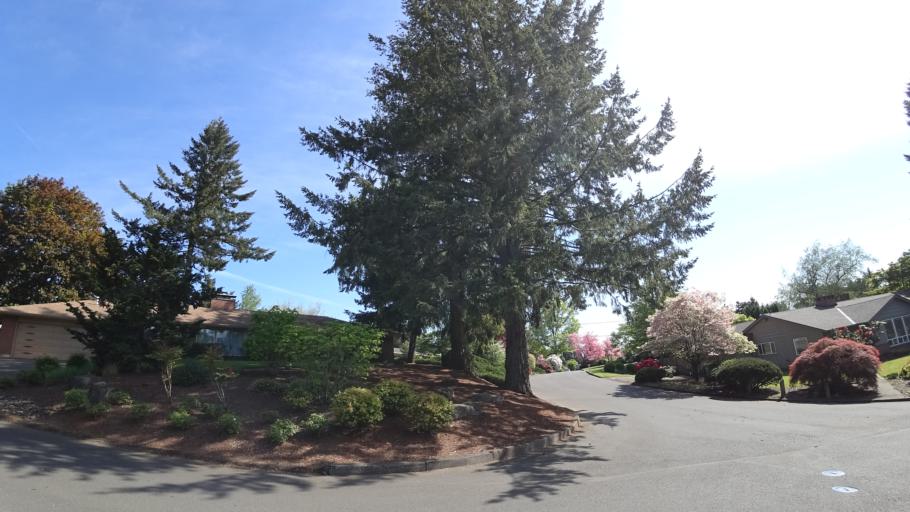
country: US
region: Oregon
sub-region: Washington County
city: West Slope
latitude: 45.4929
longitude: -122.7444
